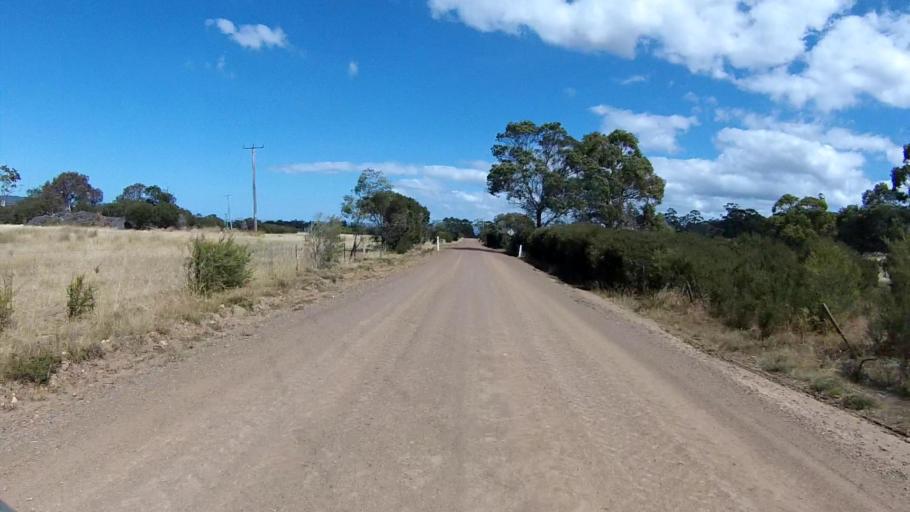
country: AU
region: Tasmania
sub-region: Break O'Day
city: St Helens
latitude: -41.9737
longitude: 148.0725
